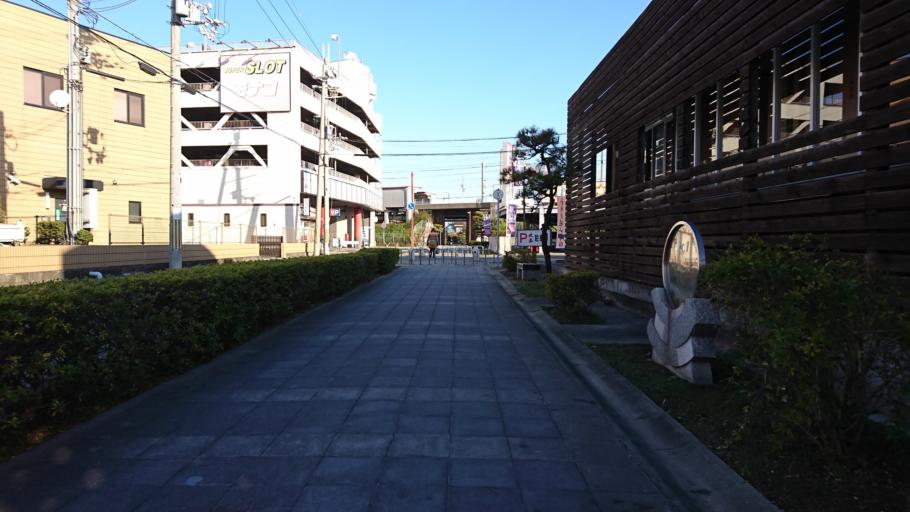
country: JP
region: Hyogo
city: Kakogawacho-honmachi
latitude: 34.7292
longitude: 134.8509
